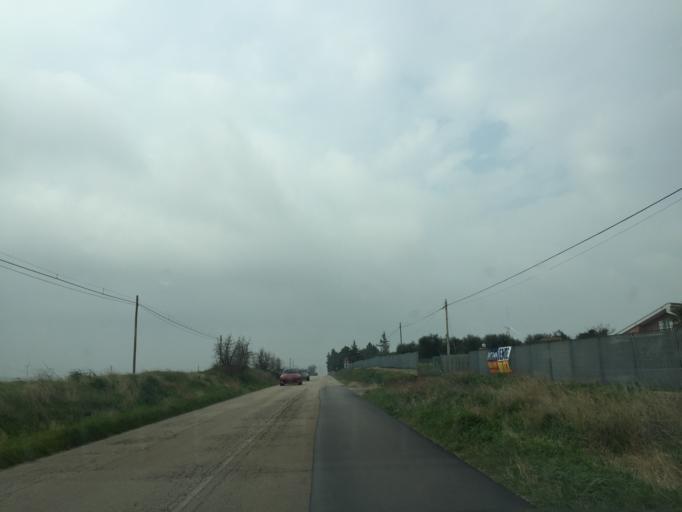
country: IT
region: Apulia
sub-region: Provincia di Foggia
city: Troia
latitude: 41.3908
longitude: 15.4042
